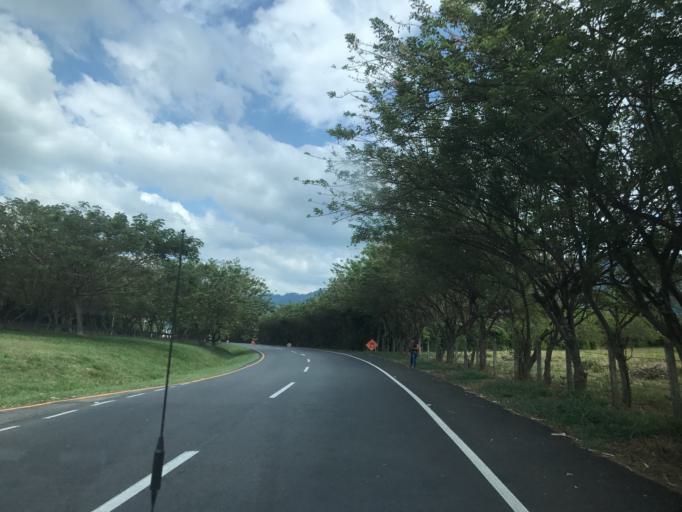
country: CO
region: Valle del Cauca
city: Obando
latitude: 4.6170
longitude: -75.9455
